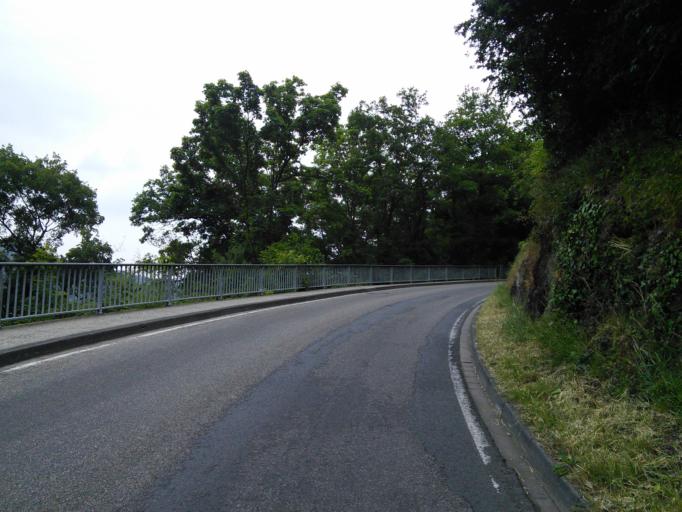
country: DE
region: Rheinland-Pfalz
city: Oberwesel
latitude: 50.0999
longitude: 7.7354
